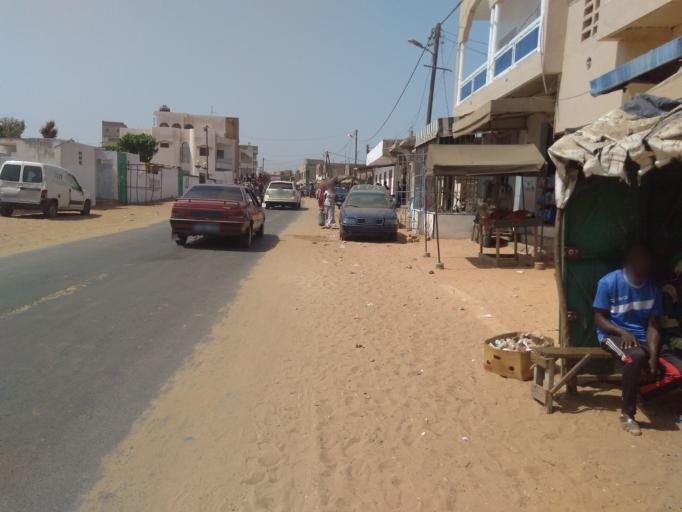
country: SN
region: Dakar
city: Pikine
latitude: 14.7954
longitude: -17.3367
